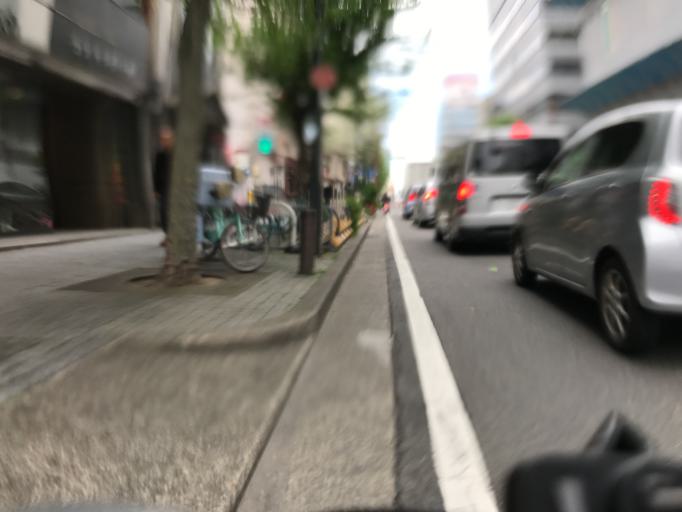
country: JP
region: Aichi
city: Nagoya-shi
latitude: 35.1663
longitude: 136.8972
